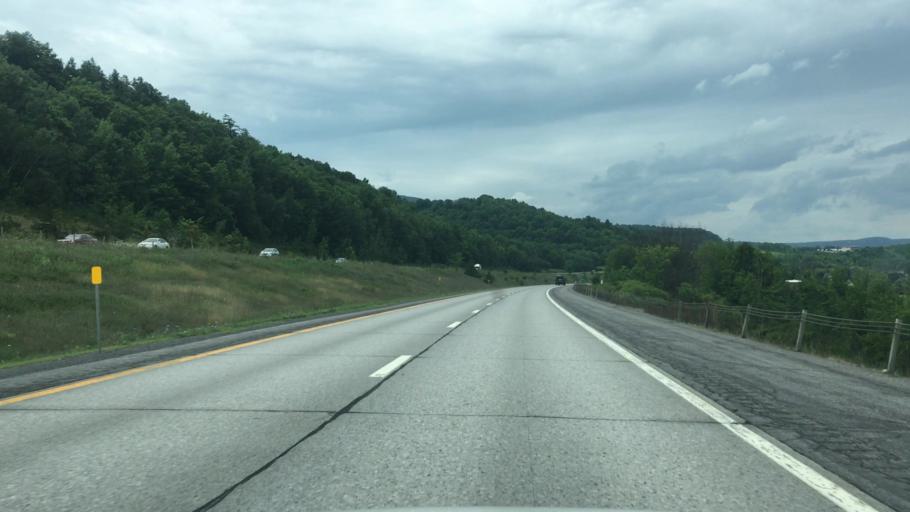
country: US
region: New York
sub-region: Schoharie County
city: Schoharie
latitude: 42.6808
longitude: -74.3758
